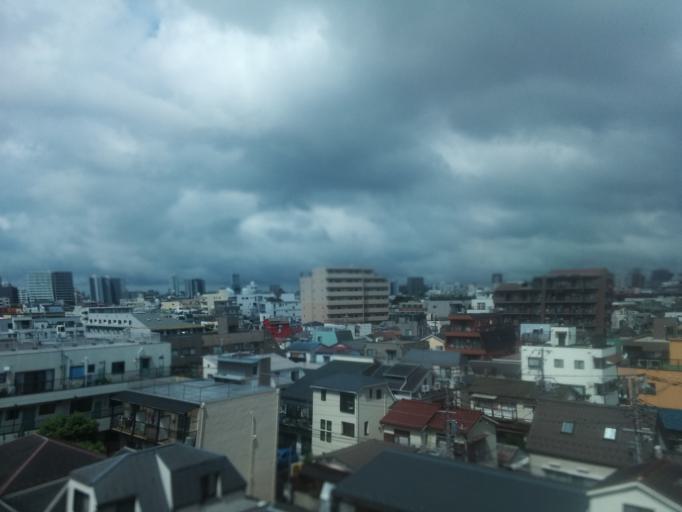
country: JP
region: Kanagawa
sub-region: Kawasaki-shi
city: Kawasaki
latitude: 35.6012
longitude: 139.7212
